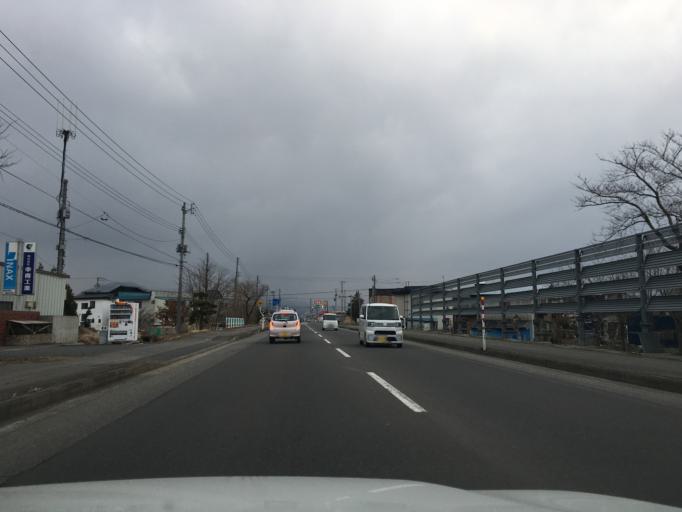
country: JP
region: Aomori
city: Kuroishi
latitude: 40.5886
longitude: 140.5690
